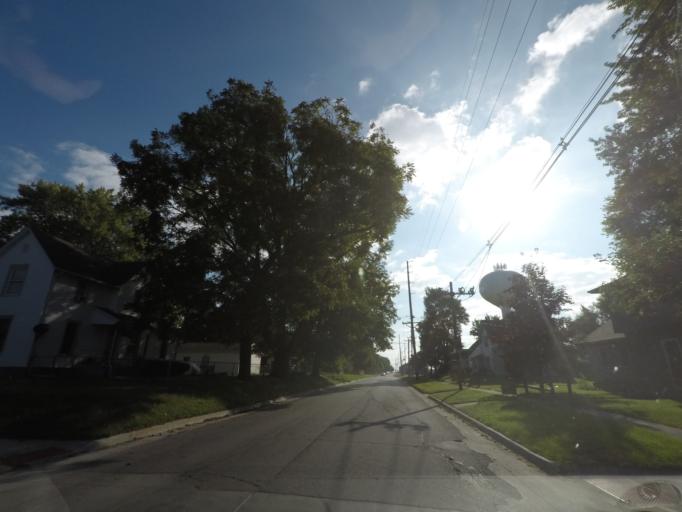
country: US
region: Iowa
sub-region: Story County
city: Nevada
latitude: 42.0156
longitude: -93.4509
